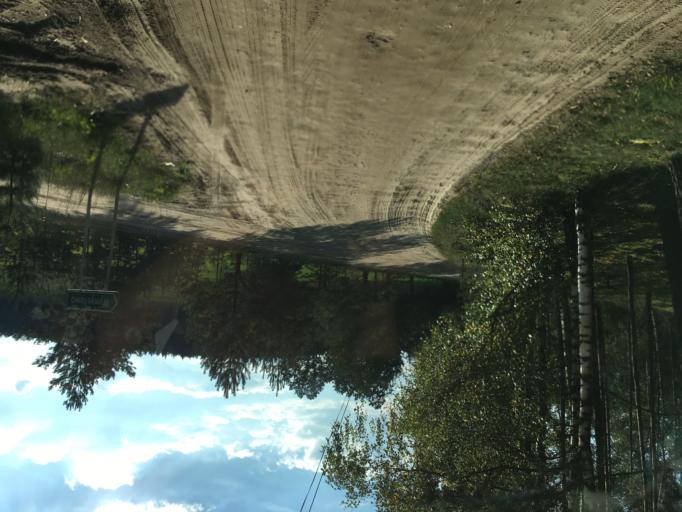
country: PL
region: Kujawsko-Pomorskie
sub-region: Powiat tucholski
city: Tuchola
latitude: 53.6040
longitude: 17.9105
